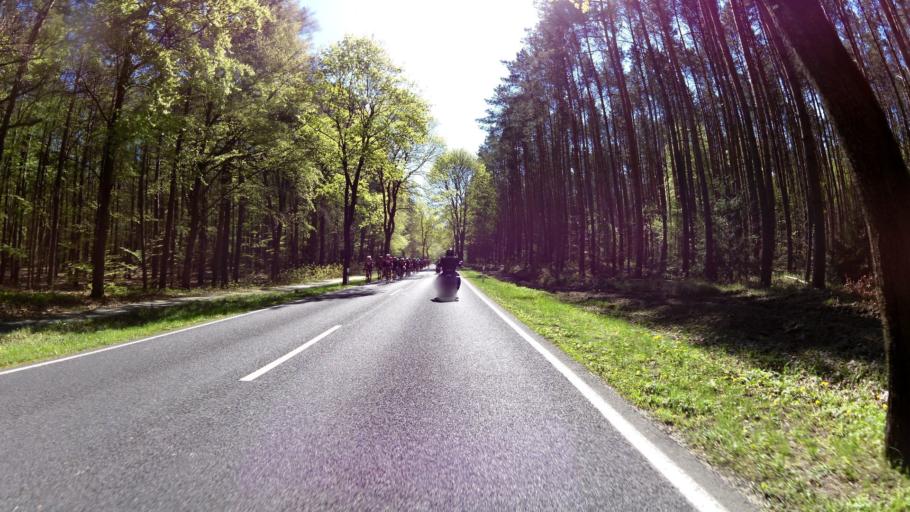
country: DE
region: Brandenburg
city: Wandlitz
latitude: 52.7227
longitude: 13.5162
